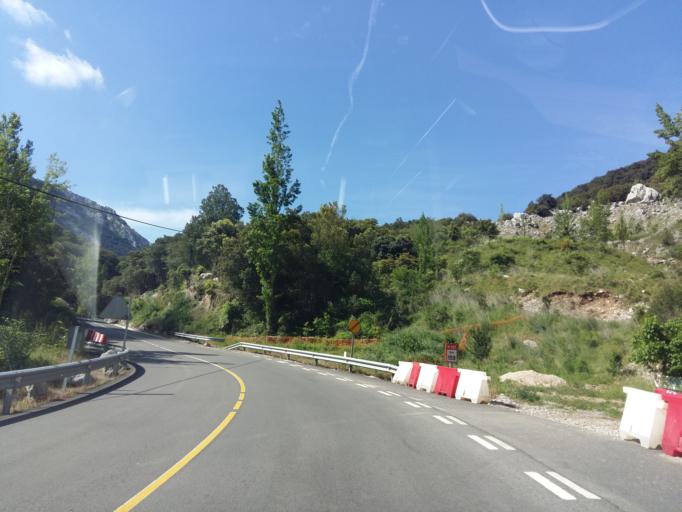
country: ES
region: Cantabria
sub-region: Provincia de Cantabria
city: Potes
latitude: 43.2244
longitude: -4.5860
